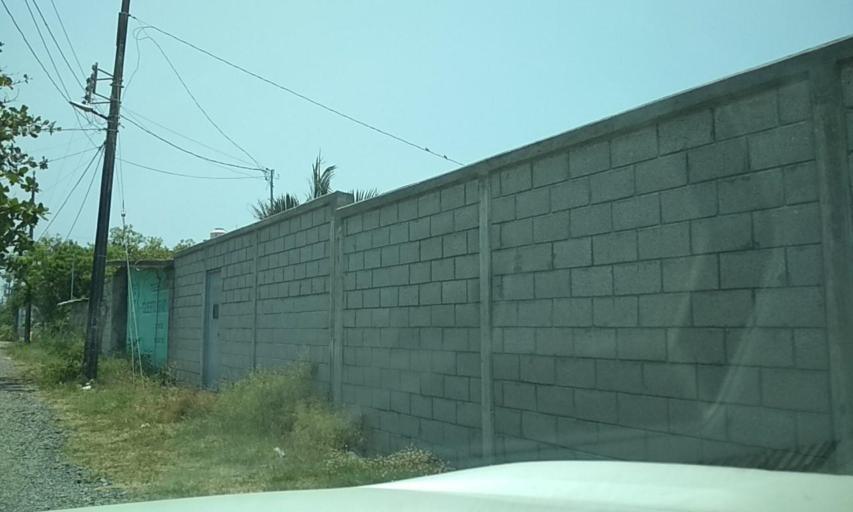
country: MX
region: Veracruz
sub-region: Veracruz
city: Las Amapolas
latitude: 19.1596
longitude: -96.1877
